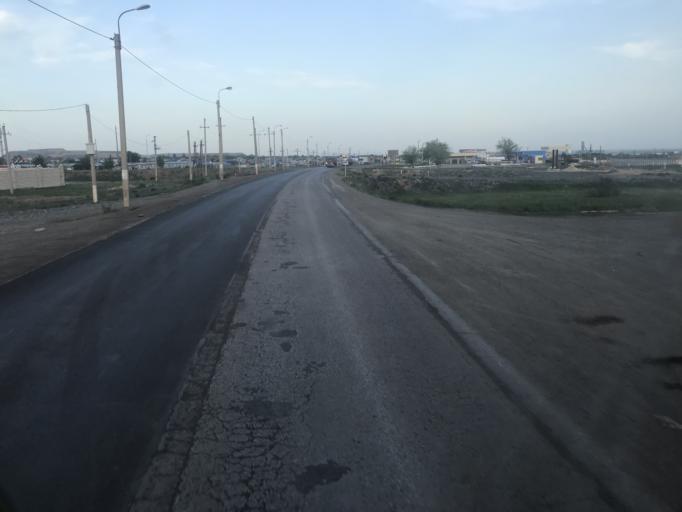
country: KZ
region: Aqtoebe
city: Khromtau
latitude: 50.2581
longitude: 58.4106
